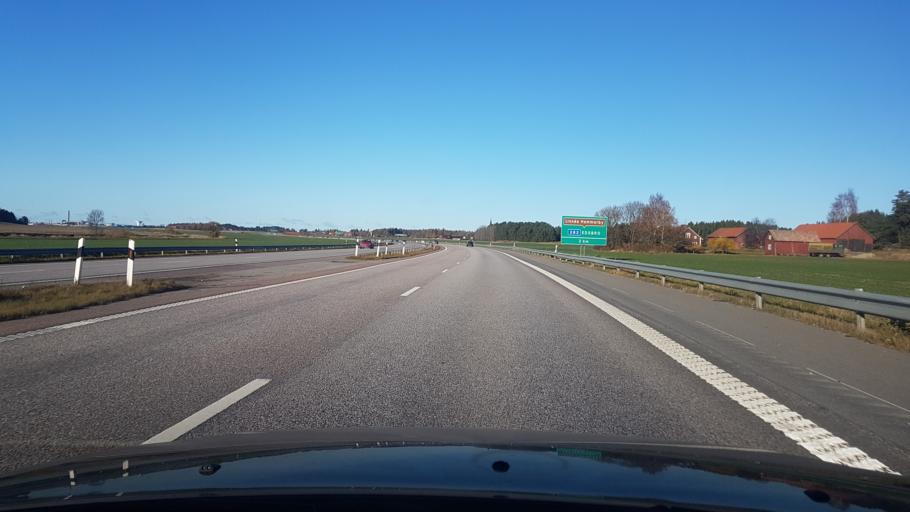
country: SE
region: Uppsala
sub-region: Uppsala Kommun
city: Saevja
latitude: 59.8172
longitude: 17.7542
